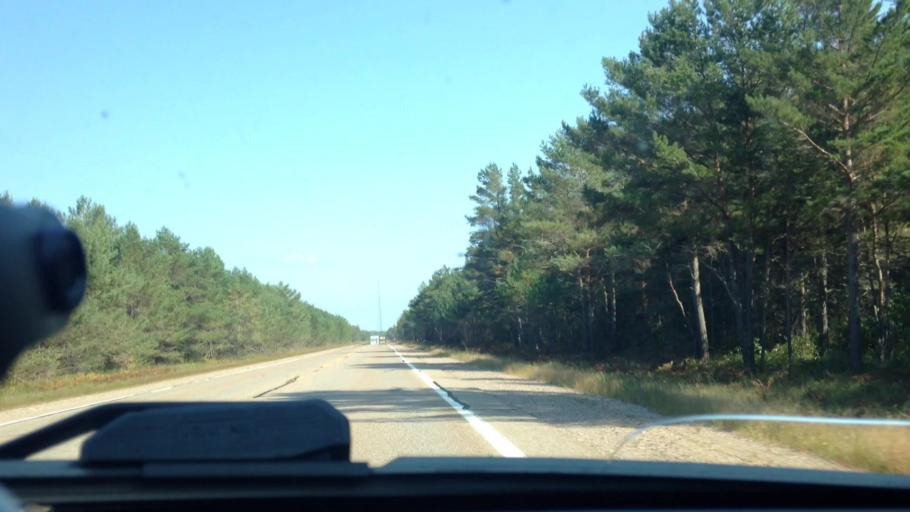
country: US
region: Michigan
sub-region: Chippewa County
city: Sault Ste. Marie
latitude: 46.3588
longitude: -84.8158
